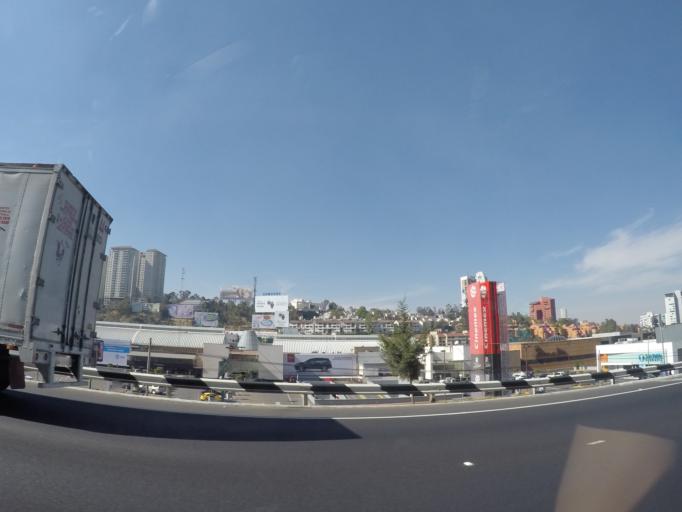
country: MX
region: Mexico City
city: Col. Bosques de las Lomas
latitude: 19.3611
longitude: -99.2707
